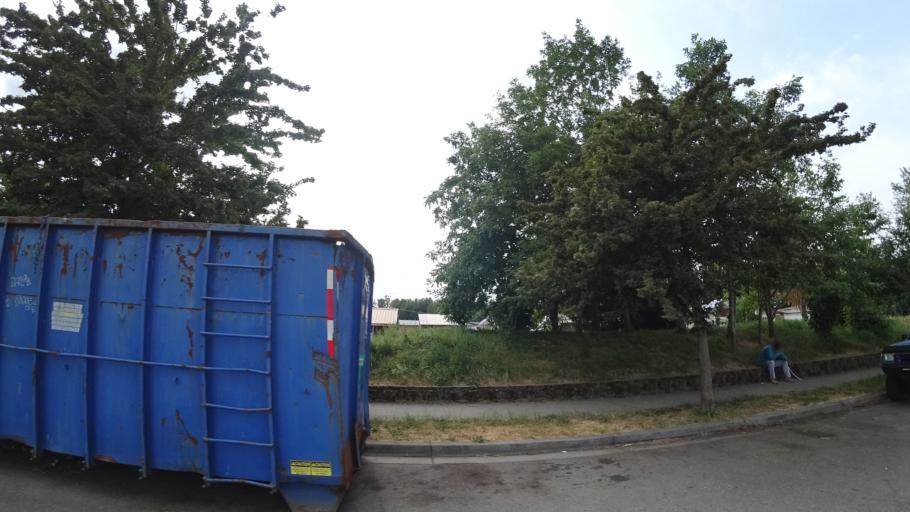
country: US
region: Washington
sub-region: Clark County
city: Vancouver
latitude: 45.5916
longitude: -122.6358
